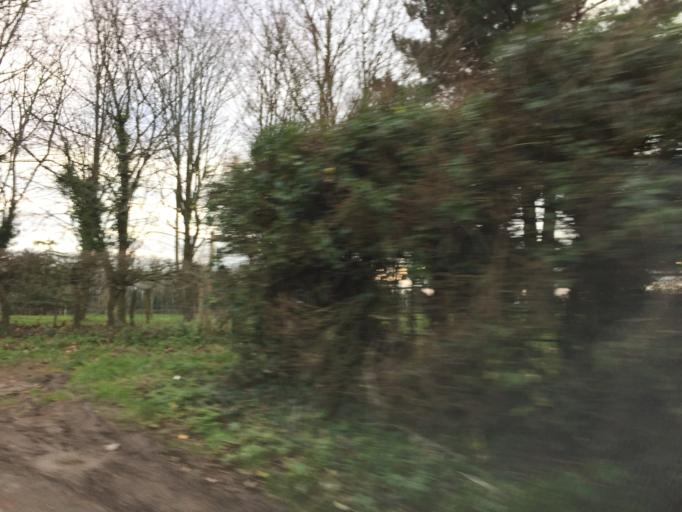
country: GB
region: Wales
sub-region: Monmouthshire
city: Rogiet
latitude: 51.5975
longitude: -2.7740
